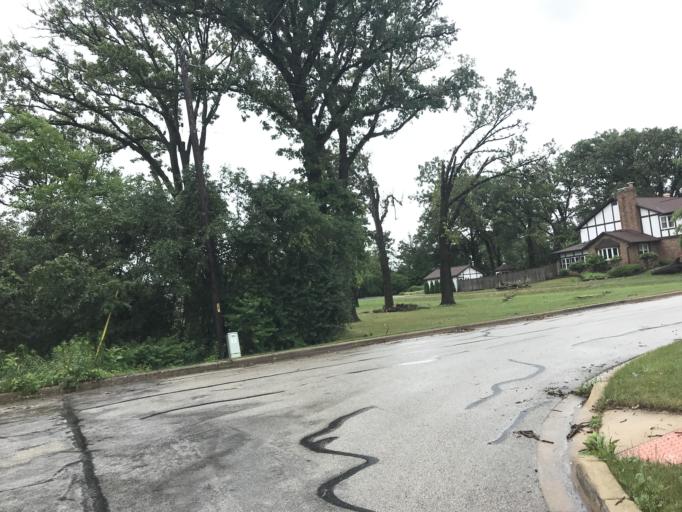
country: US
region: Illinois
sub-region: DuPage County
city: Woodridge
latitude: 41.7457
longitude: -88.0889
